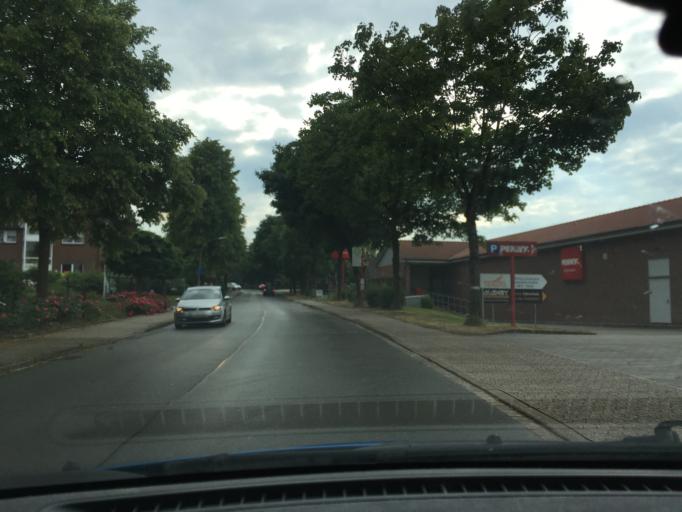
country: DE
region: Lower Saxony
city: Hollenstedt
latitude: 53.3658
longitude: 9.7140
